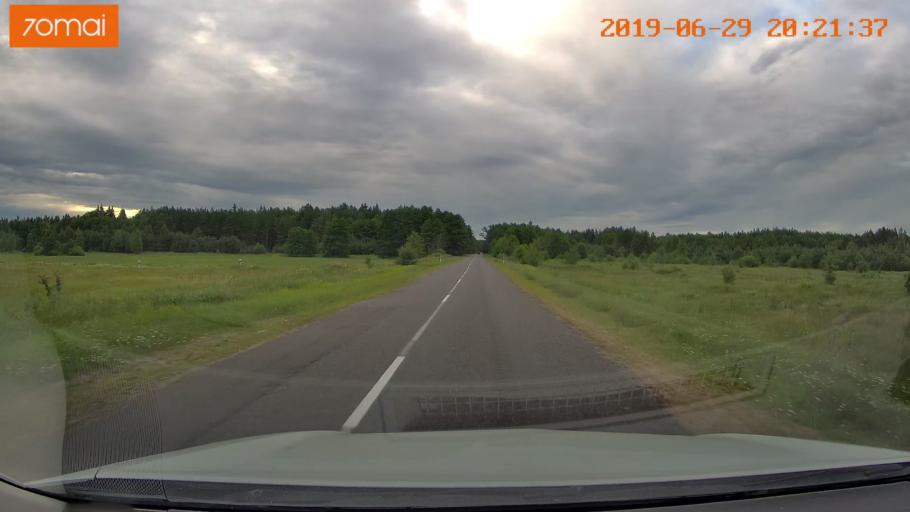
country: BY
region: Brest
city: Asnyezhytsy
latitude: 52.4218
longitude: 26.2531
